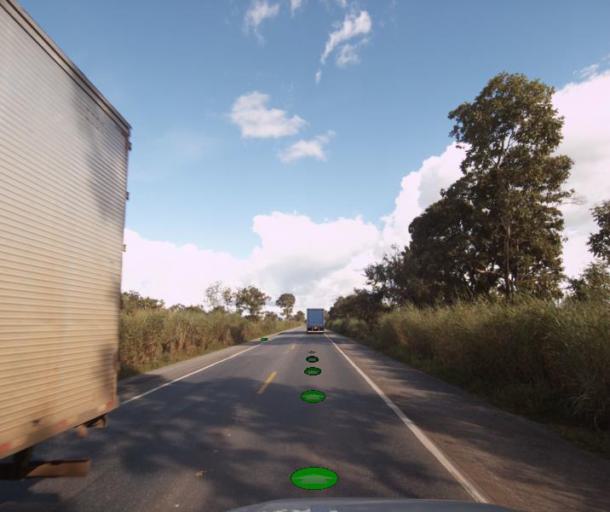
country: BR
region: Goias
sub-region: Porangatu
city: Porangatu
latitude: -13.1353
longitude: -49.1916
